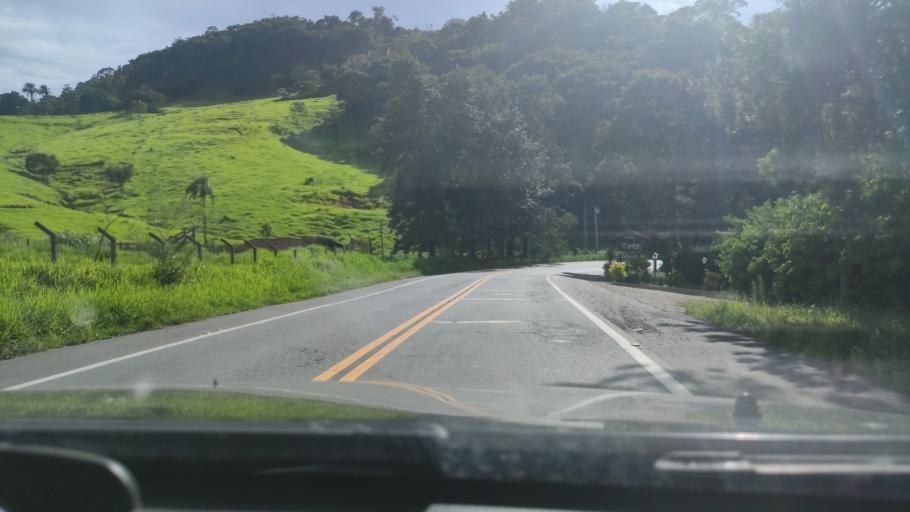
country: BR
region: Sao Paulo
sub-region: Aguas De Lindoia
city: Aguas de Lindoia
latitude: -22.5292
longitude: -46.6358
